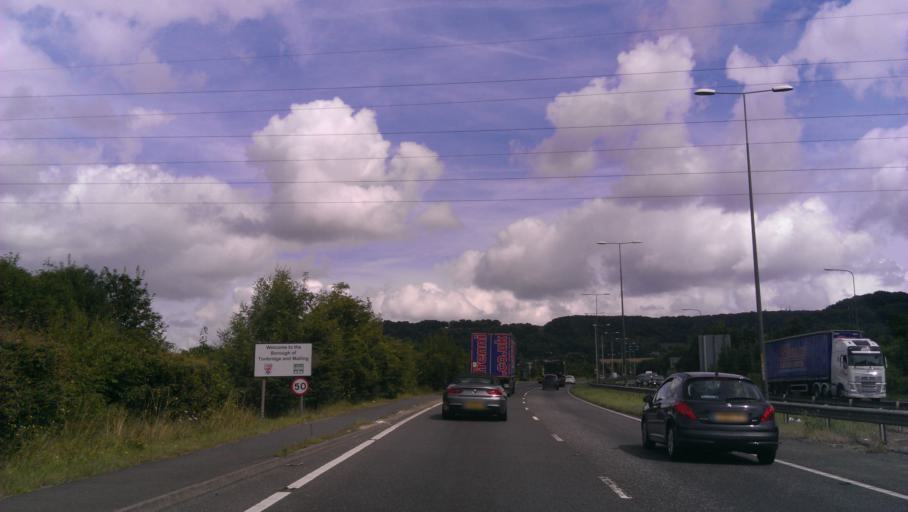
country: GB
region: England
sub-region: Kent
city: Boxley
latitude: 51.3062
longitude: 0.5120
